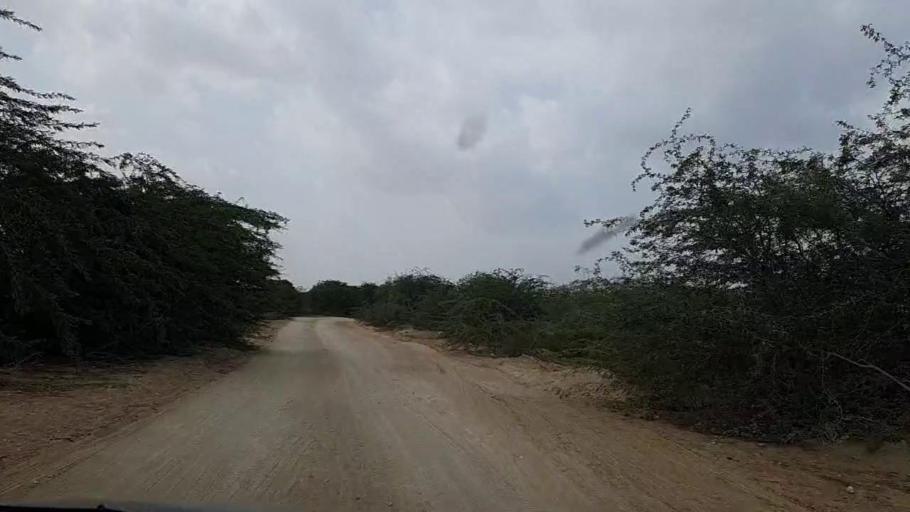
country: PK
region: Sindh
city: Kotri
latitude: 25.2790
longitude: 68.2560
